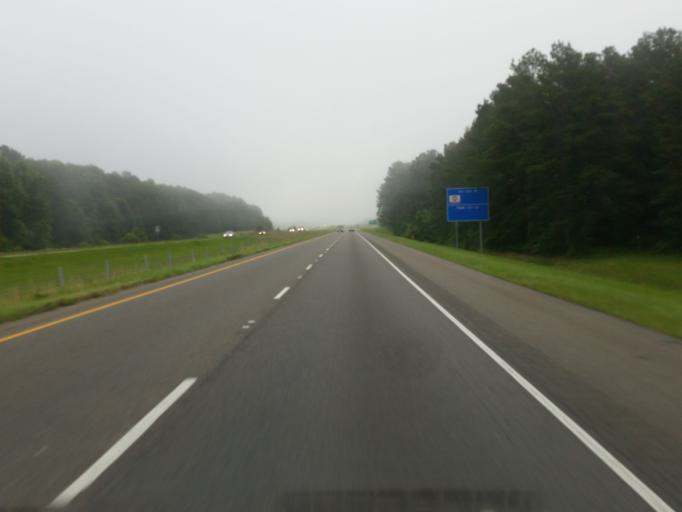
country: US
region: Louisiana
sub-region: Bossier Parish
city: Haughton
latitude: 32.5777
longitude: -93.4432
